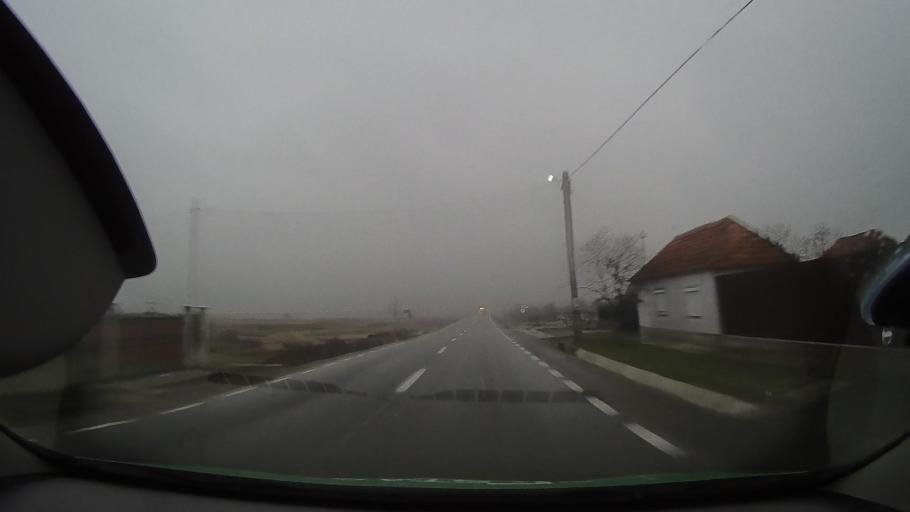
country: RO
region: Arad
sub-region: Comuna Craiova
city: Craiova
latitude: 46.6280
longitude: 21.9587
